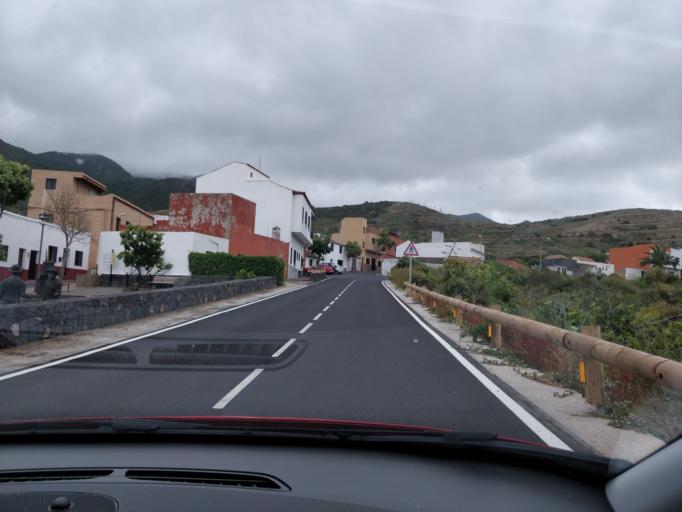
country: ES
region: Canary Islands
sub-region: Provincia de Santa Cruz de Tenerife
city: Tanque
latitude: 28.3454
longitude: -16.8464
